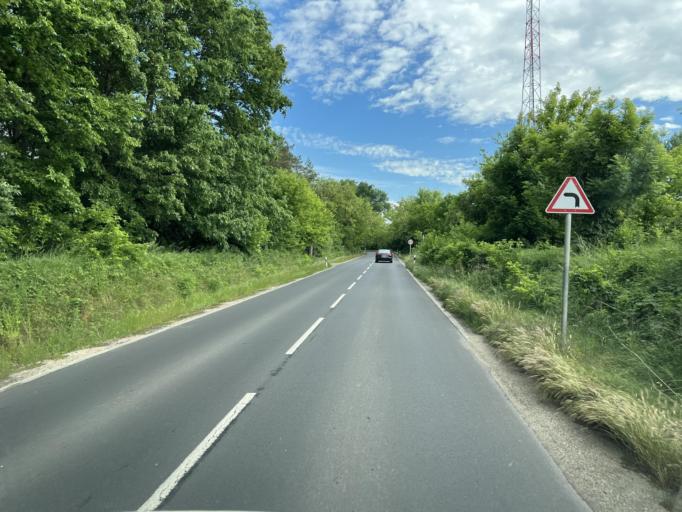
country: HU
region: Pest
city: Pecel
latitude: 47.5022
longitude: 19.3713
